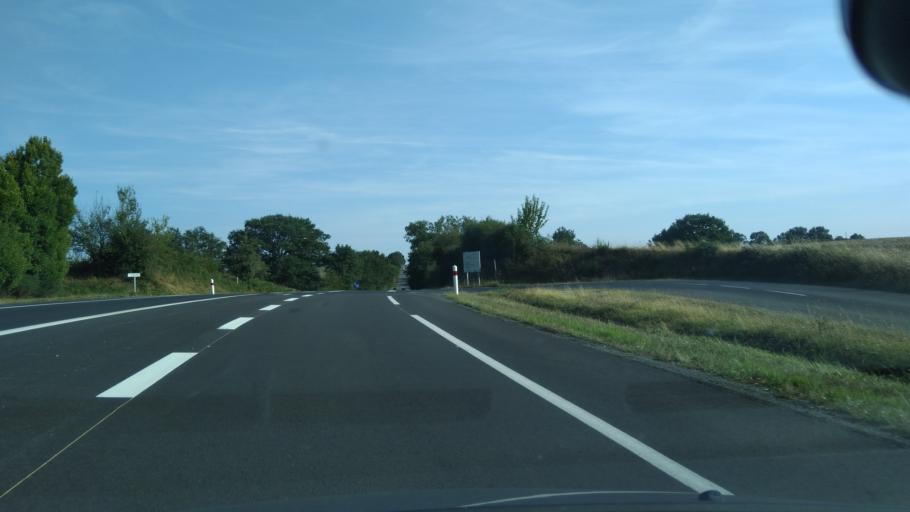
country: FR
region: Pays de la Loire
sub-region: Departement de la Mayenne
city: Entrammes
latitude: 47.9631
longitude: -0.7046
